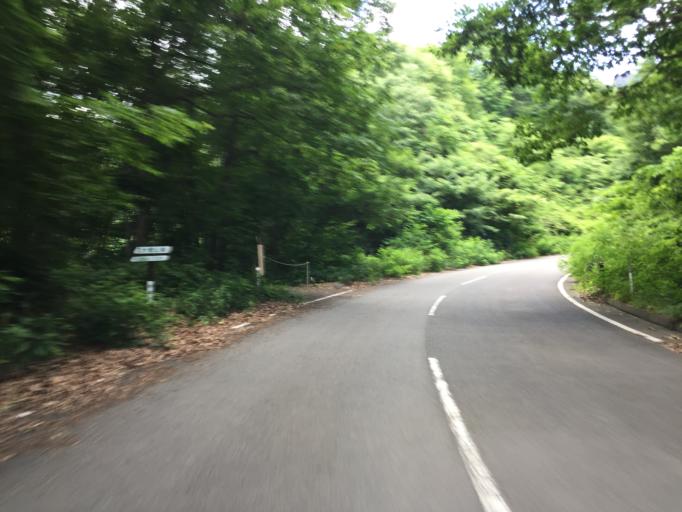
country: JP
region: Fukushima
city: Yanagawamachi-saiwaicho
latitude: 37.7586
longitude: 140.6848
